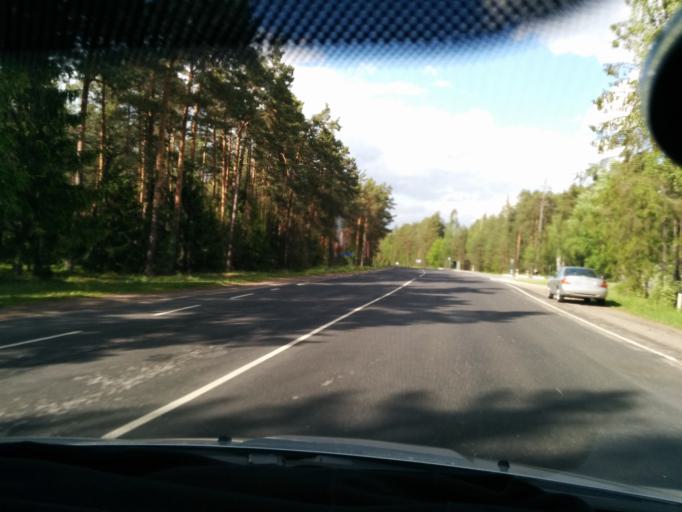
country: EE
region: Harju
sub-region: Loksa linn
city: Loksa
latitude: 59.5403
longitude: 25.7349
